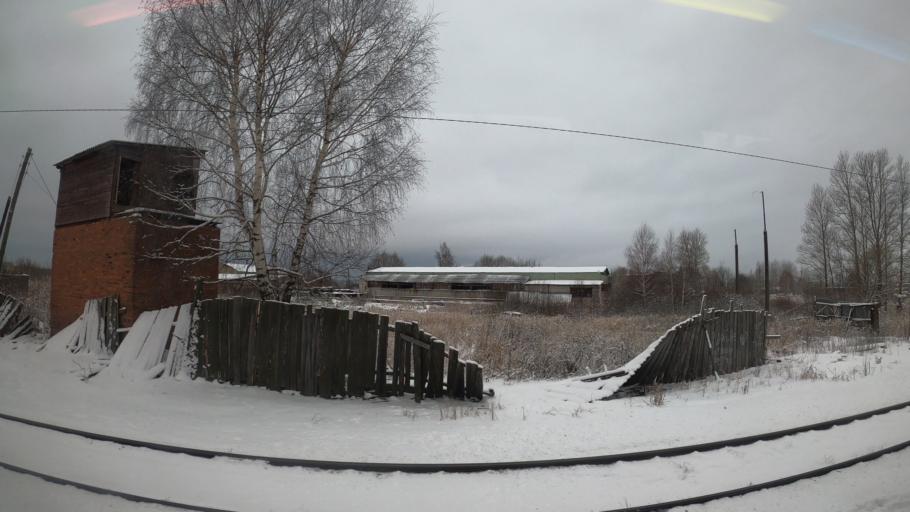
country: RU
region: Jaroslavl
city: Pereslavl'-Zalesskiy
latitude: 56.7342
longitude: 38.8934
